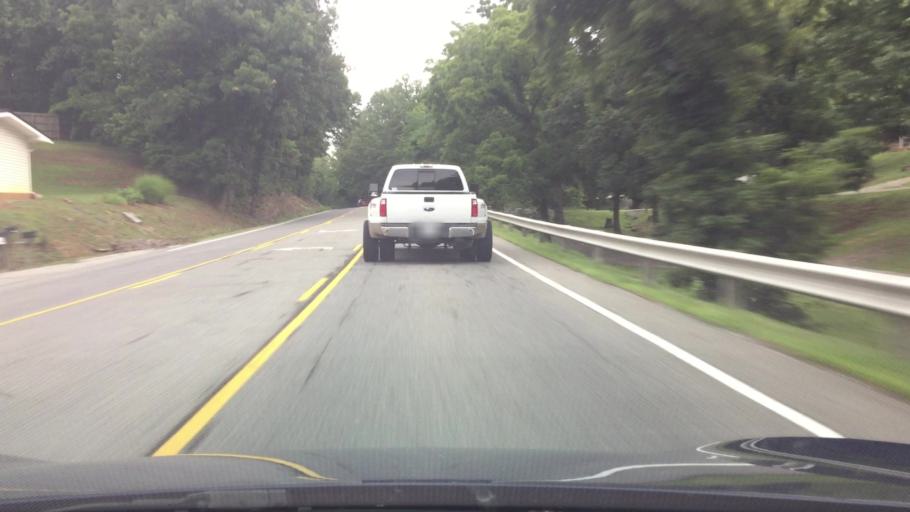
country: US
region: Virginia
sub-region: Montgomery County
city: Shawsville
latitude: 37.1411
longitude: -80.3233
